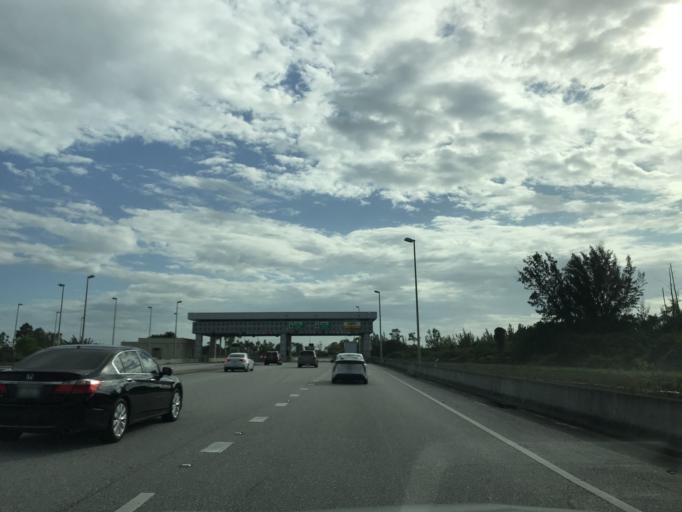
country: US
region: Florida
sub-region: Palm Beach County
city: Greenacres City
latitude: 26.6166
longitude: -80.1756
